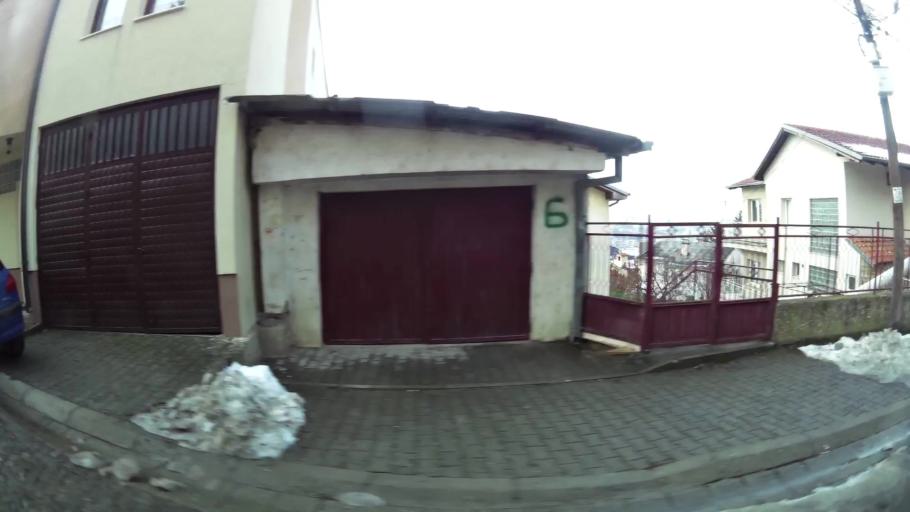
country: XK
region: Pristina
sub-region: Komuna e Prishtines
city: Pristina
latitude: 42.6680
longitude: 21.1796
